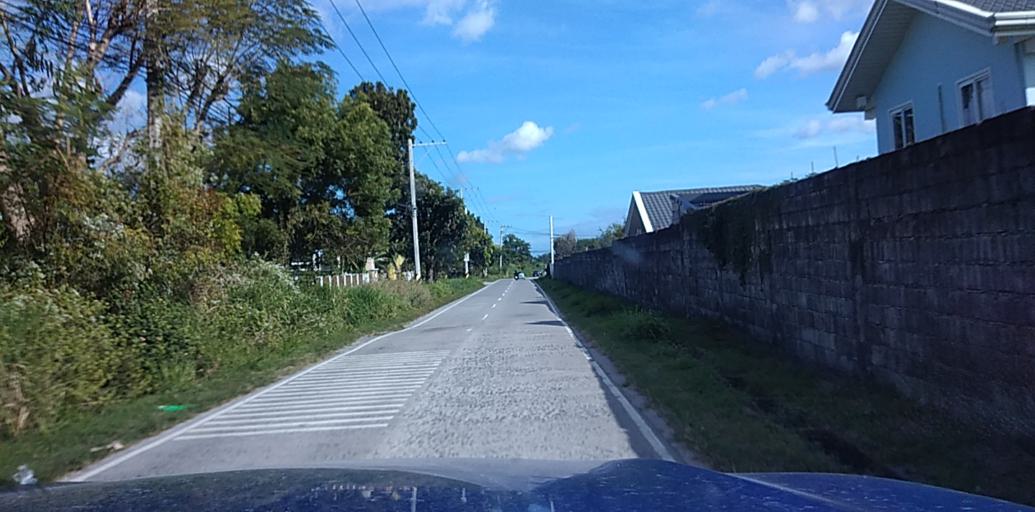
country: PH
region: Central Luzon
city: Santol
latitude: 15.1453
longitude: 120.5534
